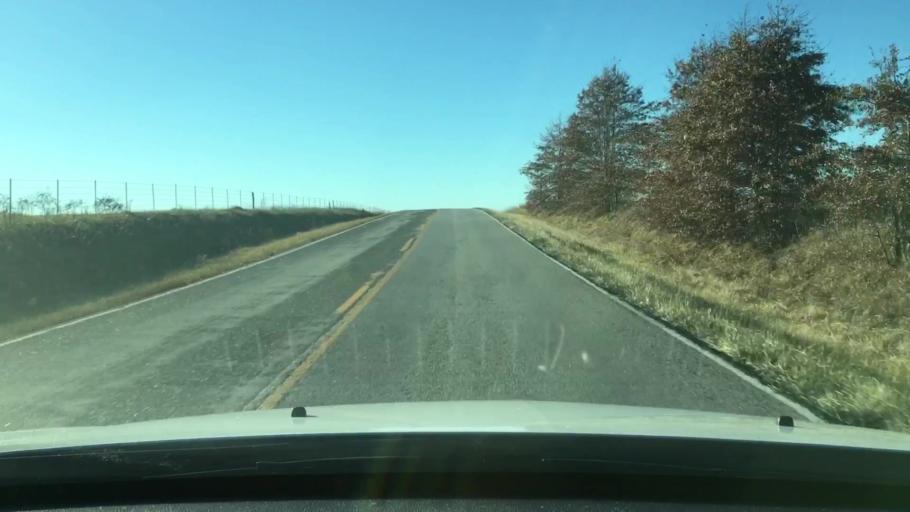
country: US
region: Missouri
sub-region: Audrain County
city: Vandalia
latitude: 39.2813
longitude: -91.6688
